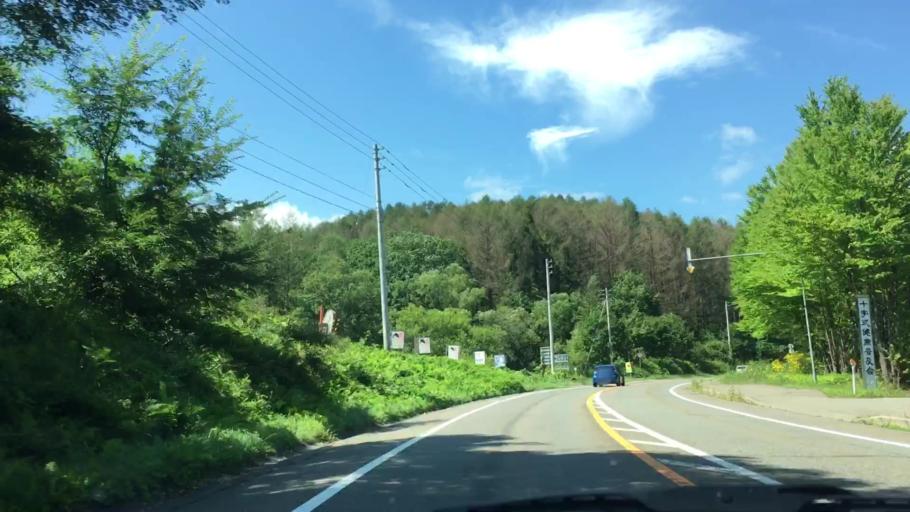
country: JP
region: Hokkaido
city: Otofuke
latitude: 43.2324
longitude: 143.5411
